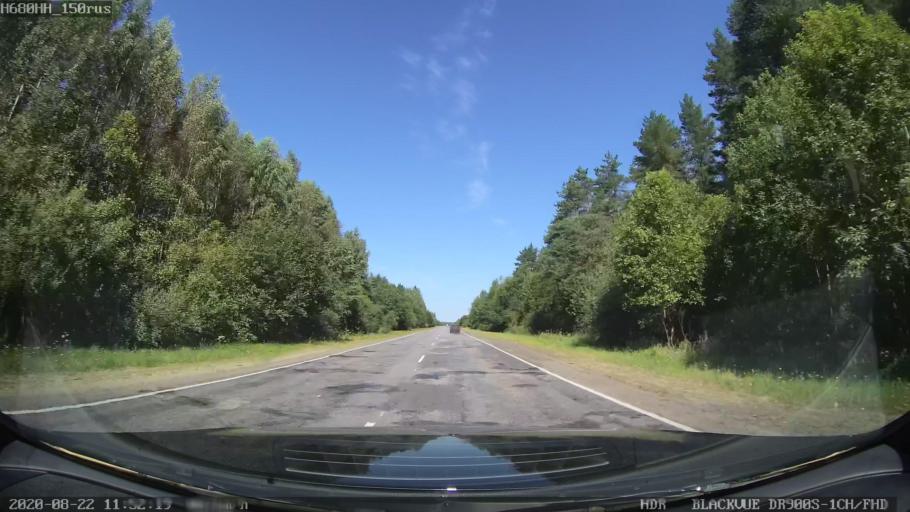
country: RU
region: Tverskaya
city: Vasil'yevskiy Mokh
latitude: 57.1139
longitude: 36.1177
